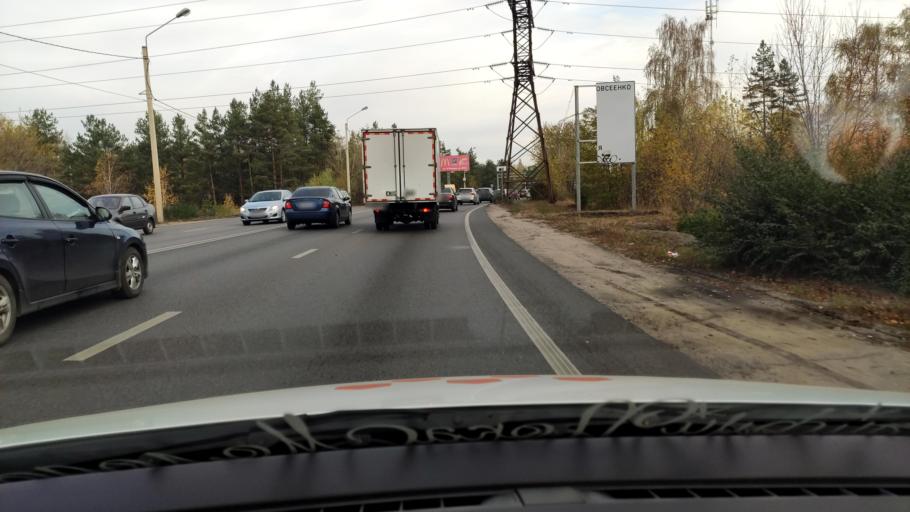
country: RU
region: Voronezj
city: Pridonskoy
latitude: 51.6791
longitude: 39.1151
